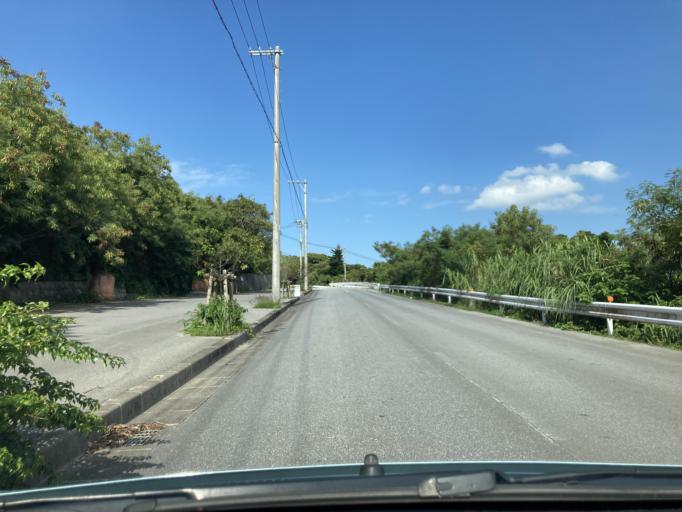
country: JP
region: Okinawa
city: Ginowan
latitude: 26.2786
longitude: 127.7984
